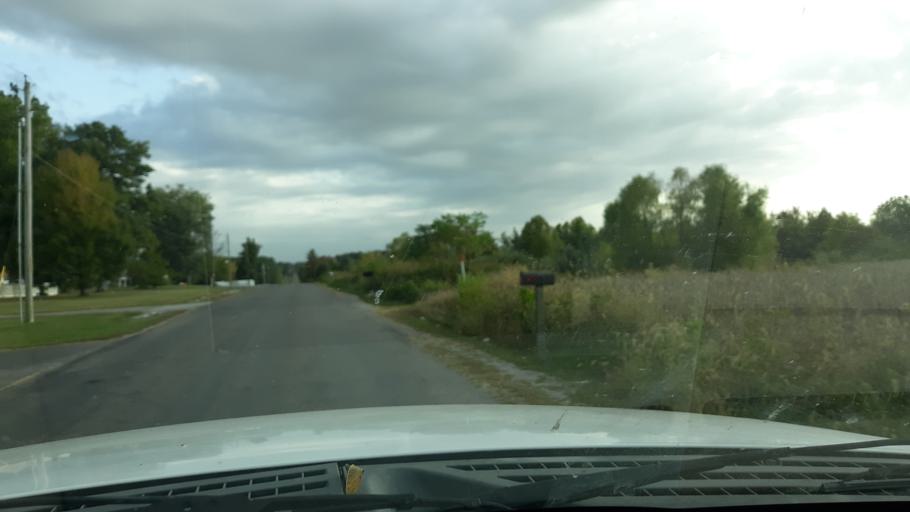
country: US
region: Illinois
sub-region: Saline County
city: Eldorado
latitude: 37.8264
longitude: -88.5026
